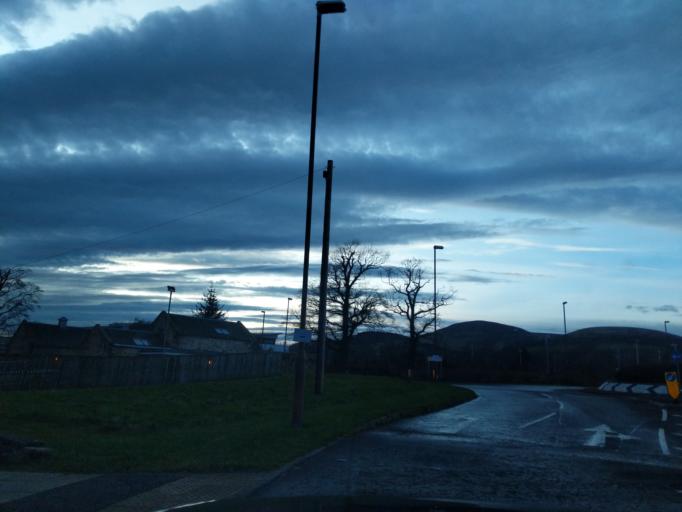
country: GB
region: Scotland
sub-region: Midlothian
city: Loanhead
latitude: 55.8667
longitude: -3.1981
